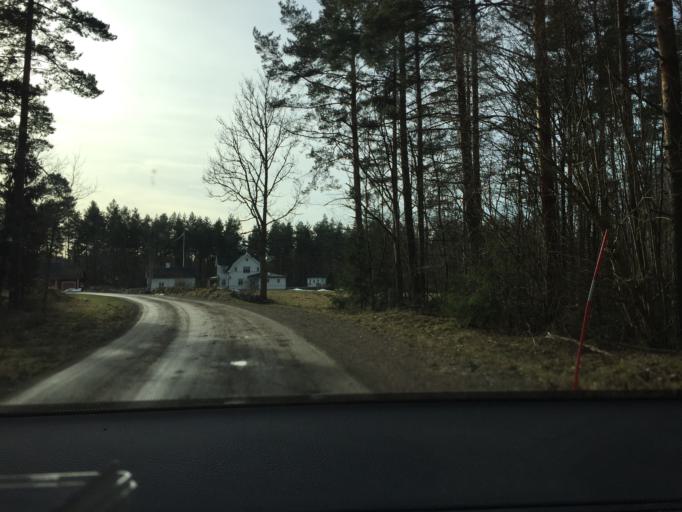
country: SE
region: OErebro
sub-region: Orebro Kommun
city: Odensbacken
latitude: 59.1163
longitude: 15.4673
